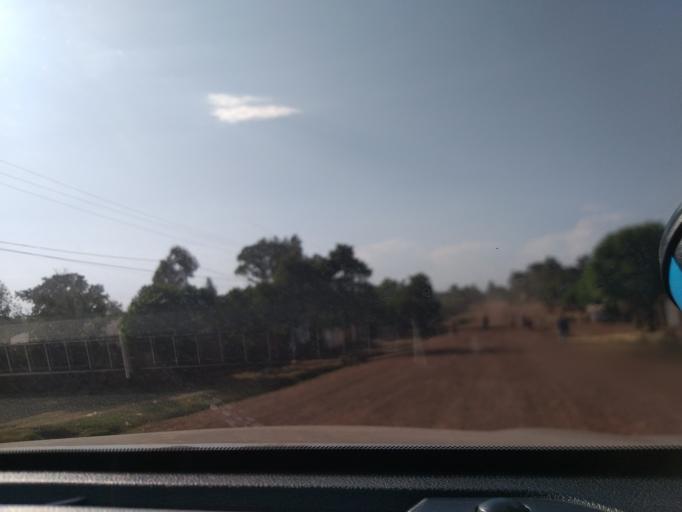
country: ET
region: Oromiya
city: Shashemene
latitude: 7.4258
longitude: 38.8137
